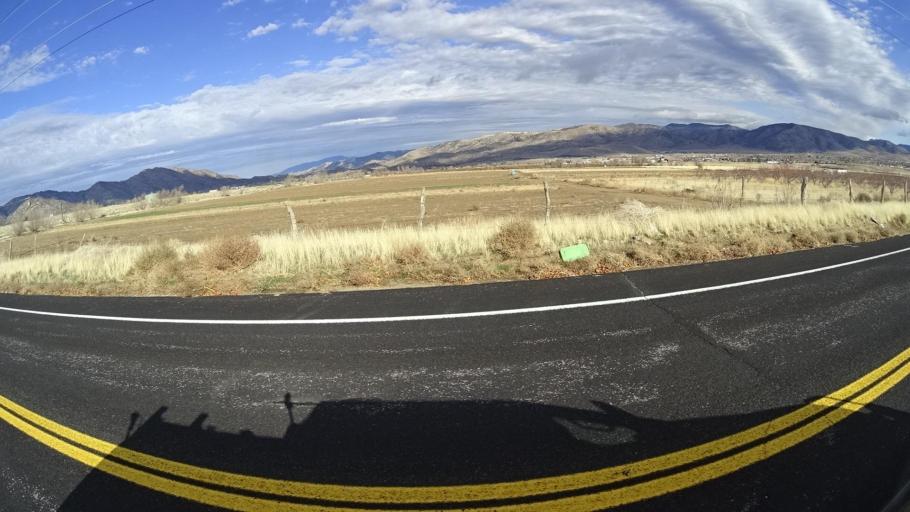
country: US
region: California
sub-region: Kern County
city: Tehachapi
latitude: 35.1094
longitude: -118.4753
